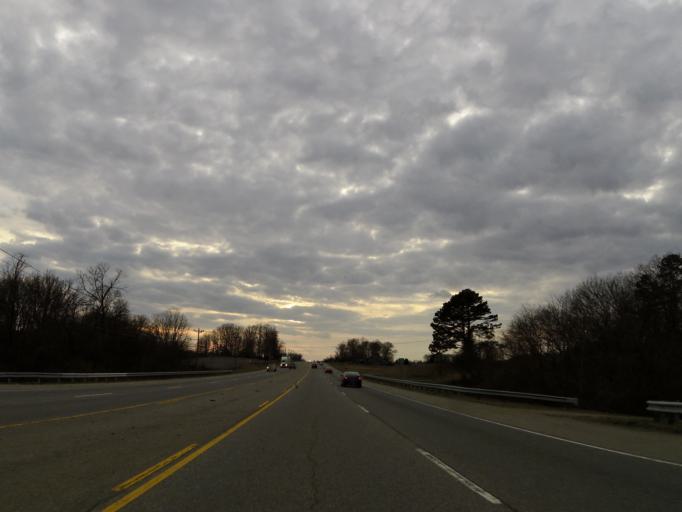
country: US
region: Tennessee
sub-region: Loudon County
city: Greenback
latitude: 35.6597
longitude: -84.1127
